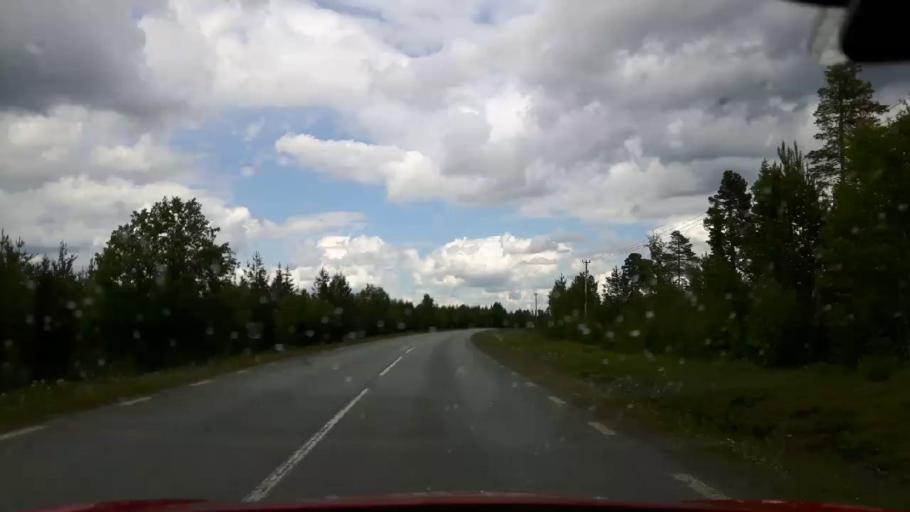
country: SE
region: Jaemtland
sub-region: Krokoms Kommun
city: Krokom
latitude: 63.5362
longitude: 14.2526
